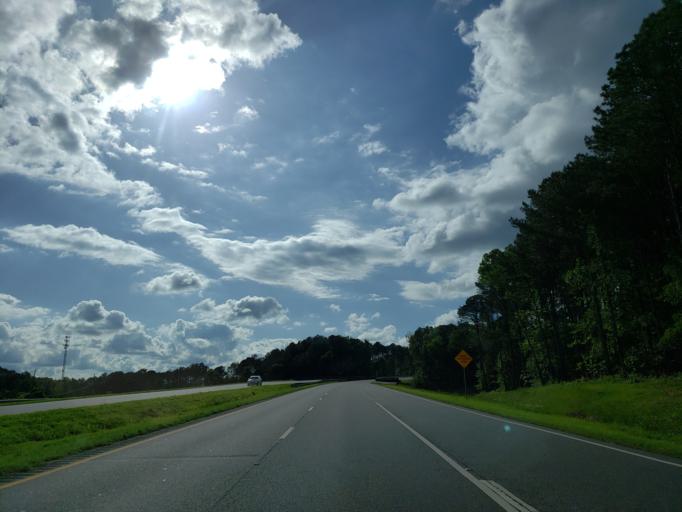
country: US
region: Georgia
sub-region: Bartow County
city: Cartersville
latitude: 34.2204
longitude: -84.8486
